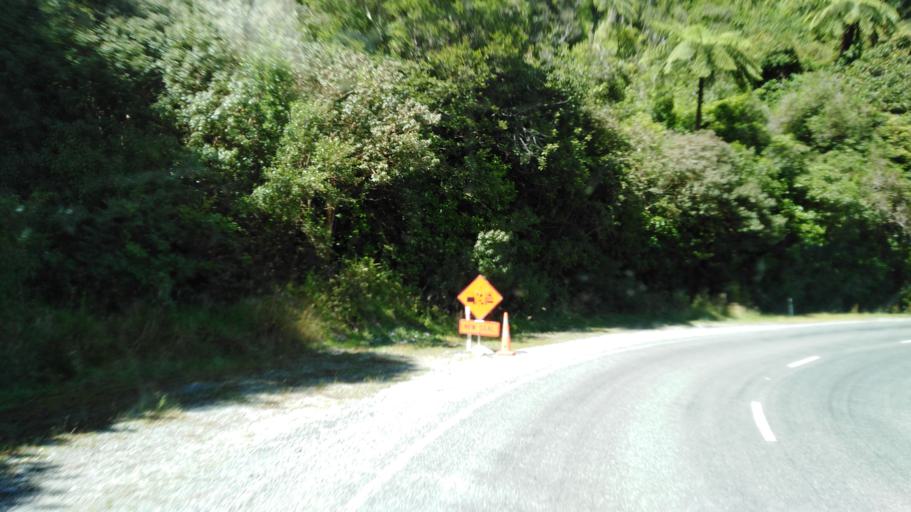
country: NZ
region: West Coast
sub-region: Buller District
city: Westport
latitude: -41.4932
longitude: 172.0501
